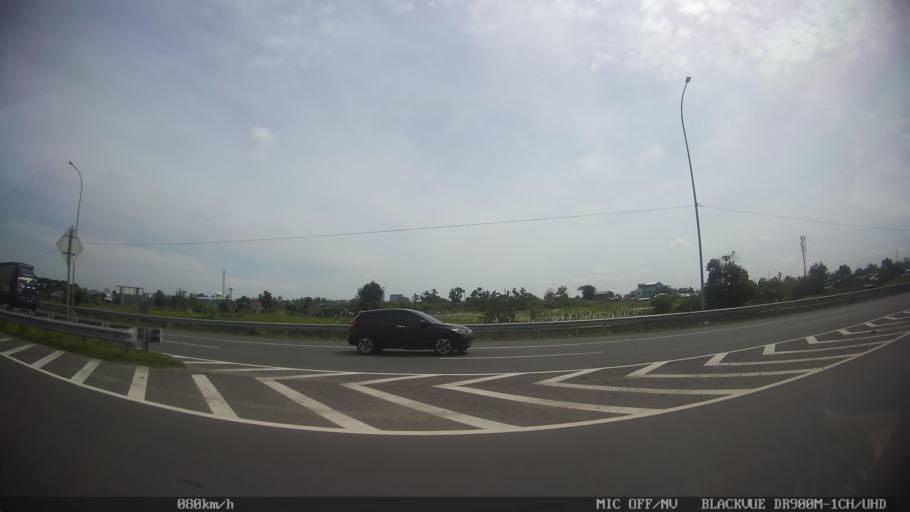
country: ID
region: North Sumatra
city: Medan
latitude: 3.6479
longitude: 98.6848
